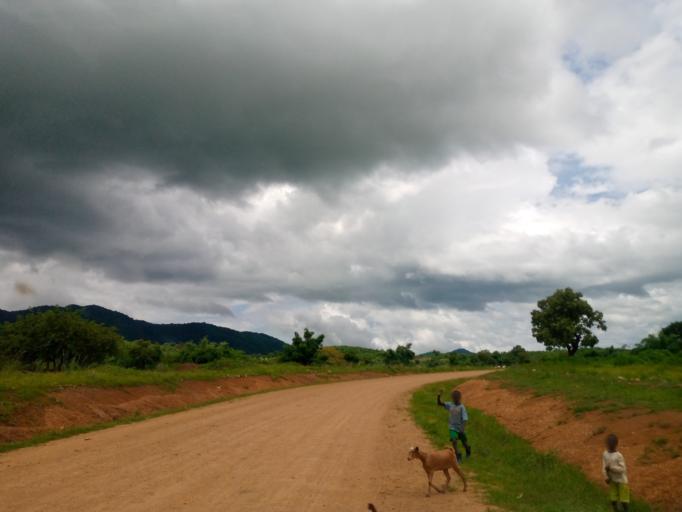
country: ET
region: Oromiya
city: Mendi
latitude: 10.2034
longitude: 35.0922
